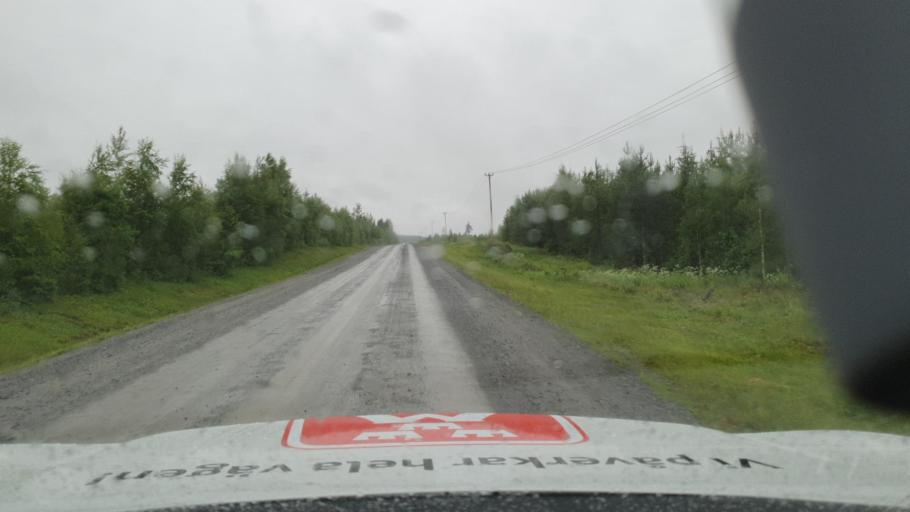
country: SE
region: Vaesterbotten
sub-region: Bjurholms Kommun
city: Bjurholm
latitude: 63.8800
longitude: 19.4401
